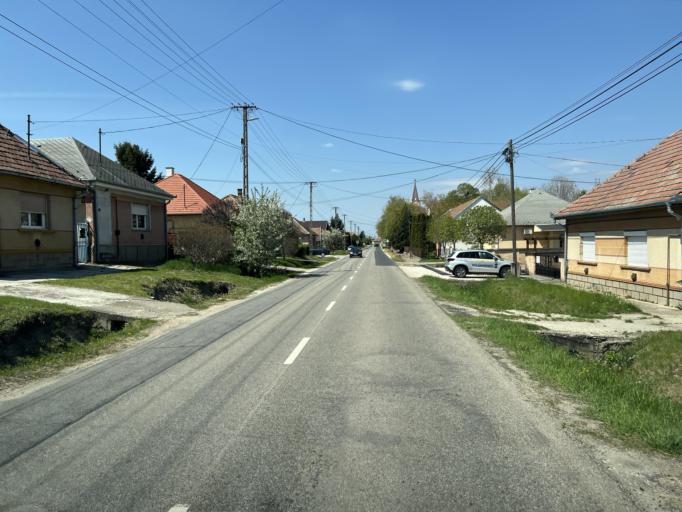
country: HU
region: Pest
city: Kakucs
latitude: 47.2400
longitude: 19.3680
